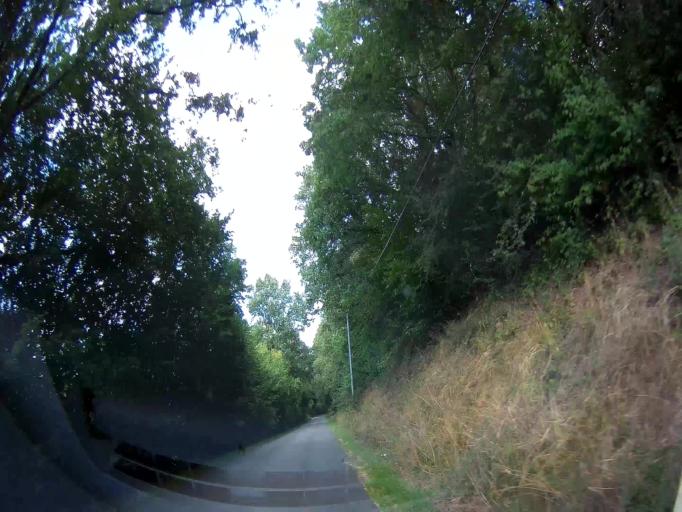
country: BE
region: Wallonia
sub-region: Province de Namur
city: Onhaye
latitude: 50.2848
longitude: 4.7919
